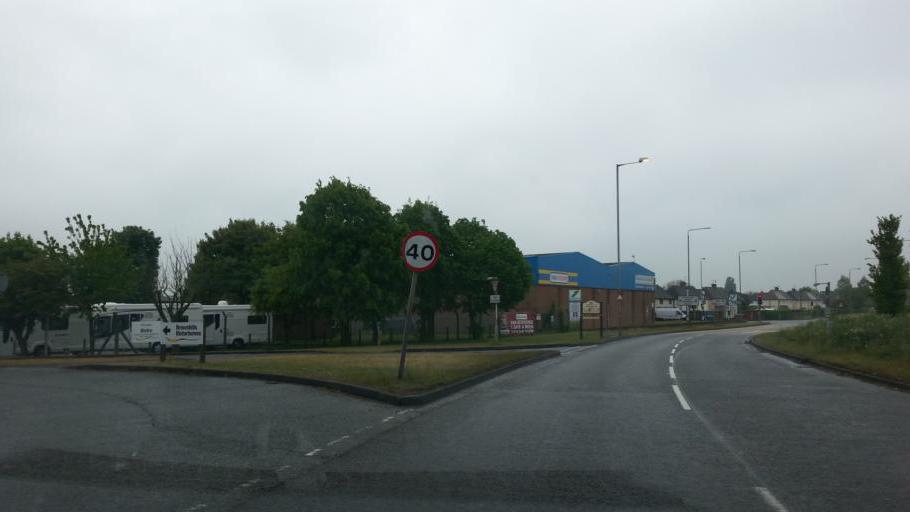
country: GB
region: England
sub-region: Nottinghamshire
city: Newark on Trent
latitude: 53.0925
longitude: -0.7888
